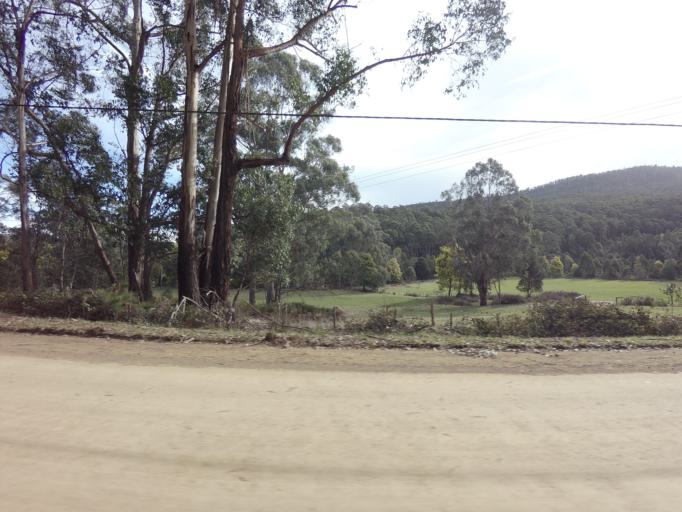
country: AU
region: Tasmania
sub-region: Huon Valley
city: Huonville
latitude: -43.0746
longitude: 147.0756
